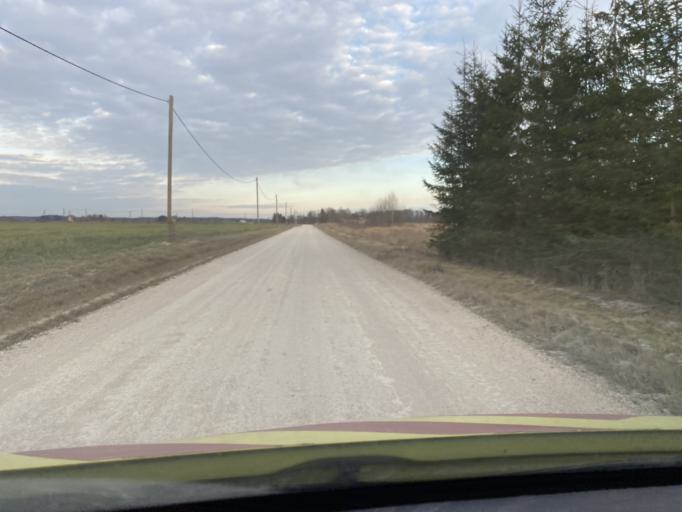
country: EE
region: Jogevamaa
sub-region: Poltsamaa linn
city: Poltsamaa
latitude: 58.5870
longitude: 26.1855
